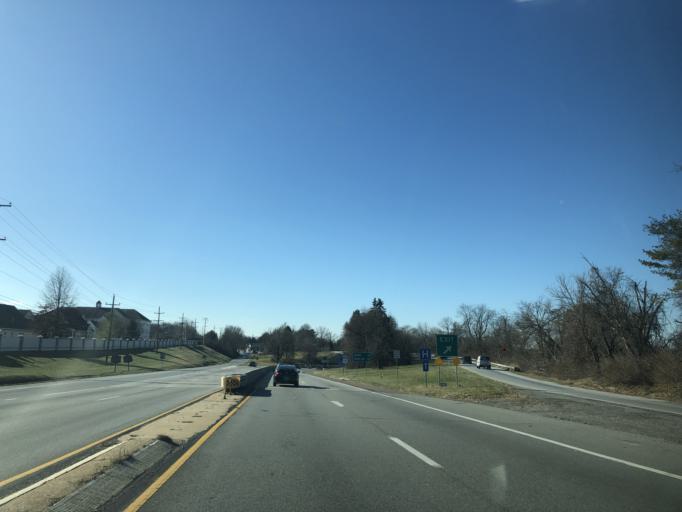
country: US
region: Pennsylvania
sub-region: Chester County
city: Kennett Square
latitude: 39.8589
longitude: -75.6890
